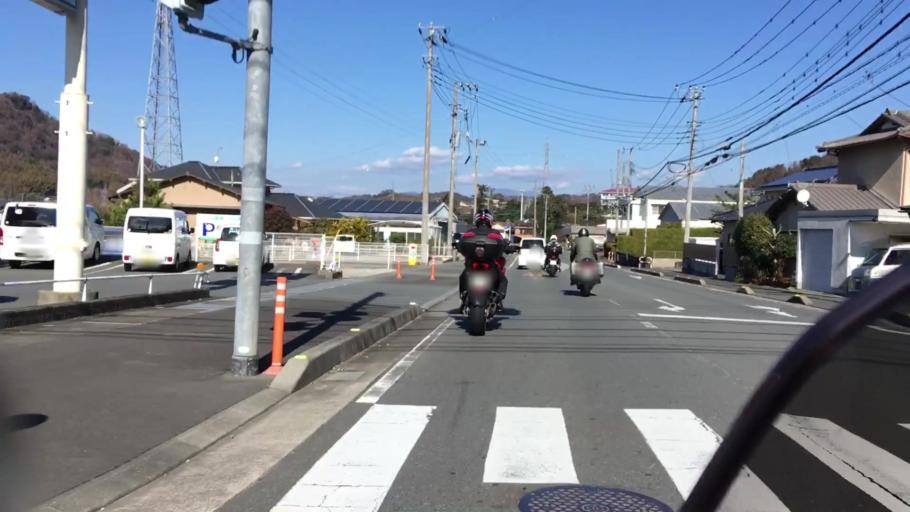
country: JP
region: Shizuoka
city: Ito
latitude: 34.9712
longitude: 138.9493
